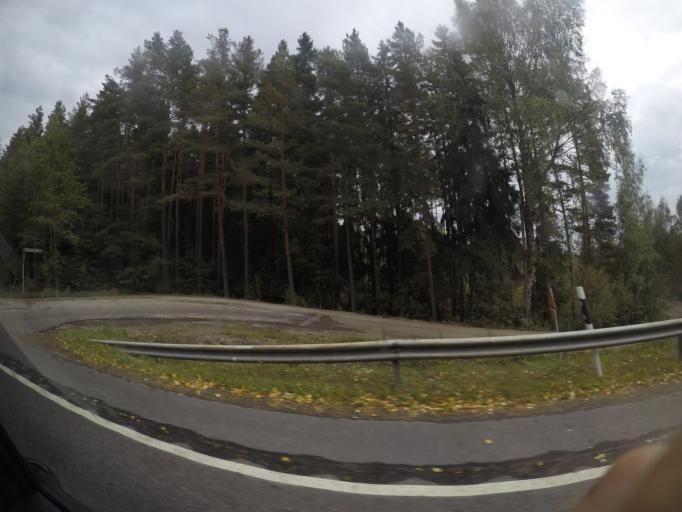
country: FI
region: Haeme
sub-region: Haemeenlinna
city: Parola
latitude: 61.0856
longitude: 24.3986
